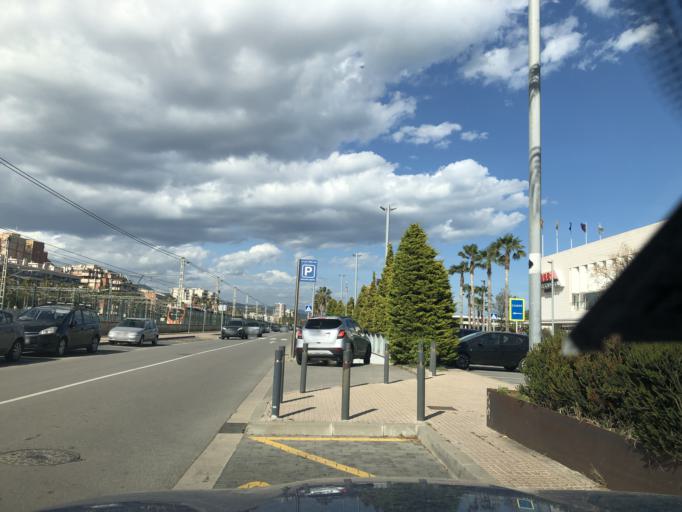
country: ES
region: Catalonia
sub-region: Provincia de Barcelona
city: Mataro
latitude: 41.5307
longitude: 2.4430
